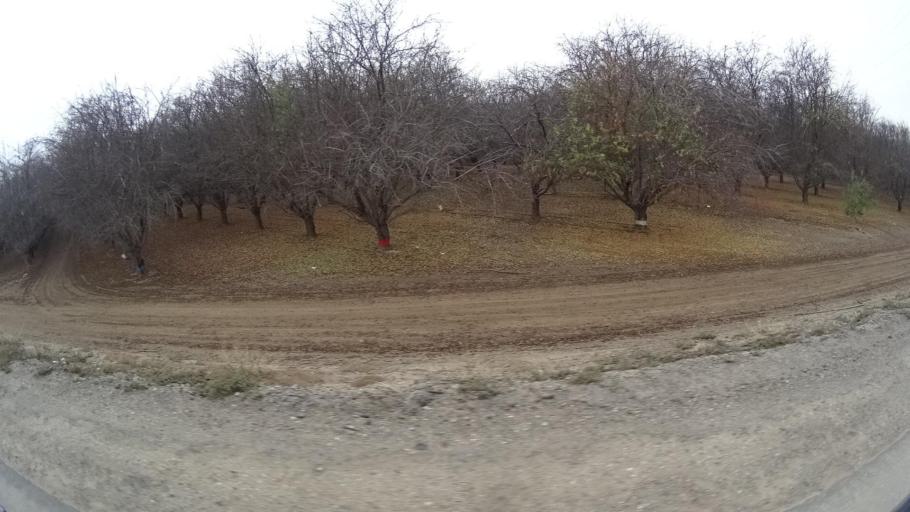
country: US
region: California
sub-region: Kern County
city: Maricopa
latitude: 35.1081
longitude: -119.3456
